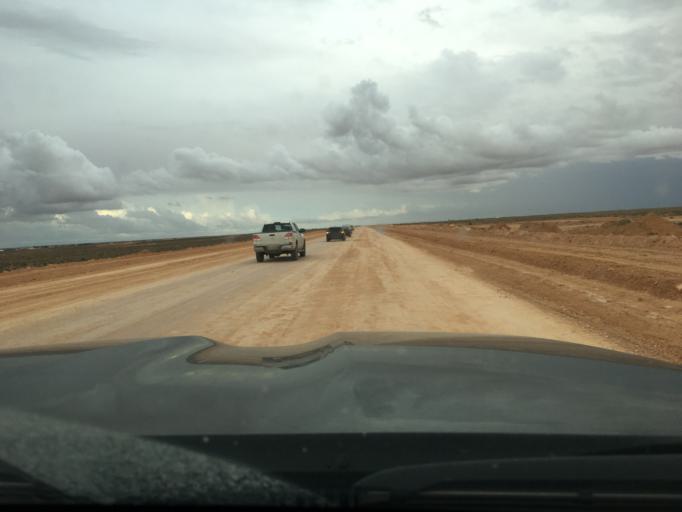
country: TN
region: Madanin
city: Medenine
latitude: 33.2713
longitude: 10.5875
